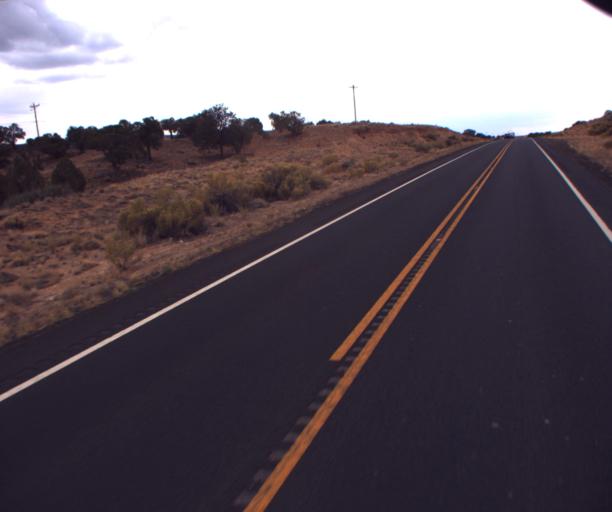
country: US
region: Arizona
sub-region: Coconino County
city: Kaibito
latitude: 36.4474
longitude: -110.7249
